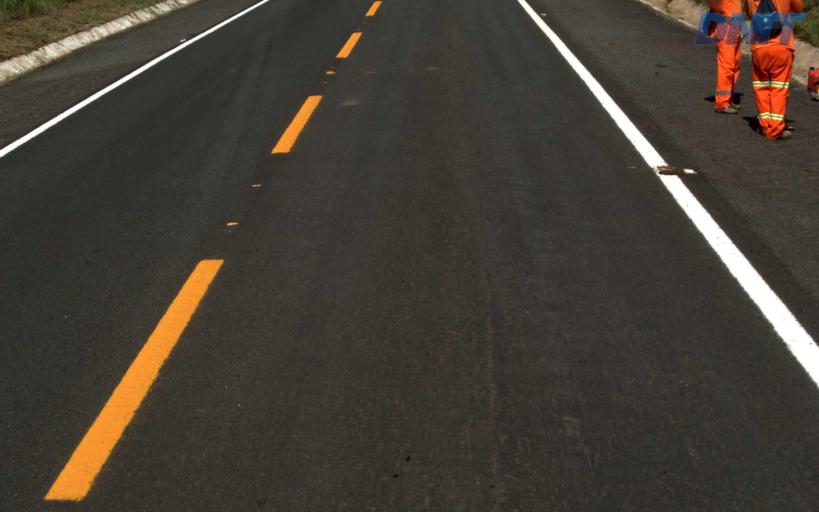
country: BR
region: Goias
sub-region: Sao Miguel Do Araguaia
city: Sao Miguel do Araguaia
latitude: -13.2900
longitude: -50.2113
